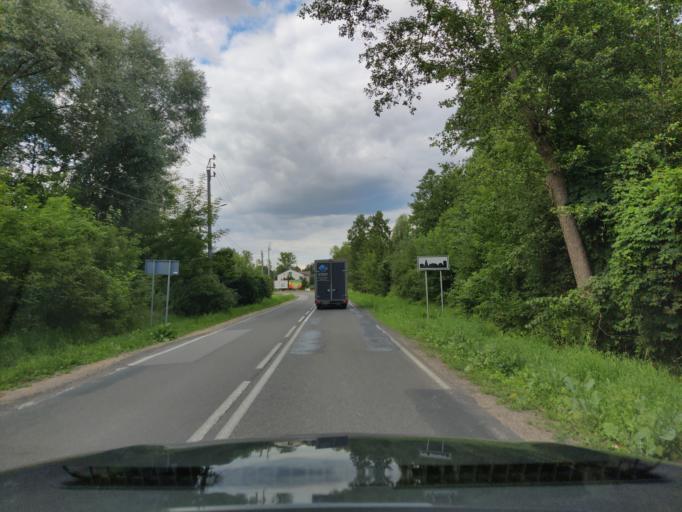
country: PL
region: Masovian Voivodeship
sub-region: Powiat sokolowski
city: Kosow Lacki
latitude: 52.5855
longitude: 22.1533
